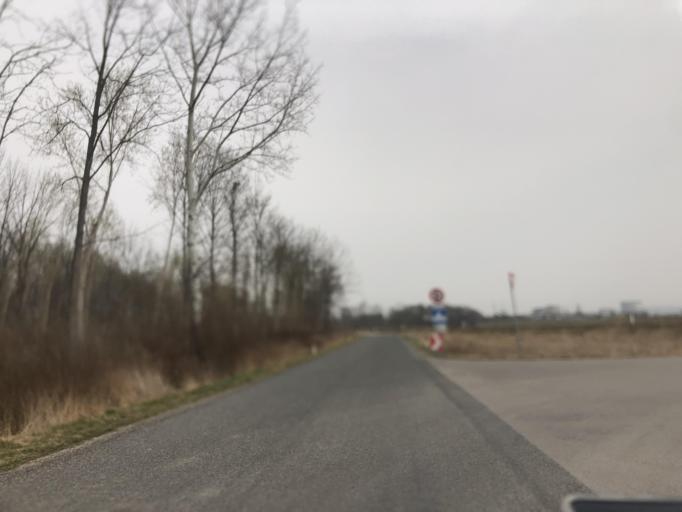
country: AT
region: Lower Austria
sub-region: Politischer Bezirk Tulln
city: Langenrohr
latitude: 48.3254
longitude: 16.0164
